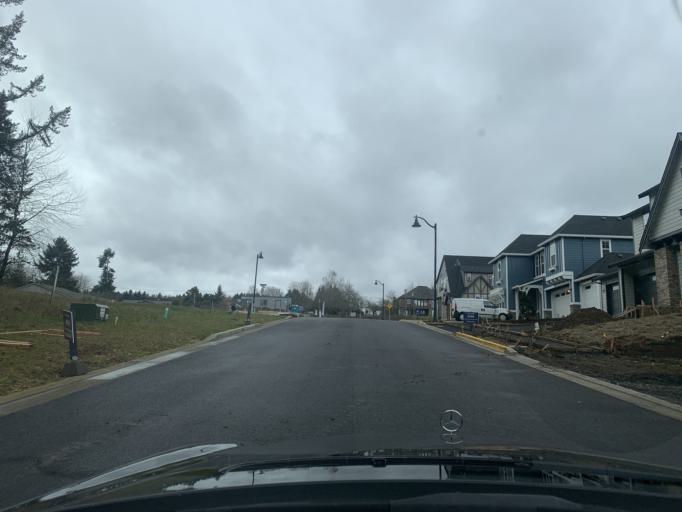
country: US
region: Oregon
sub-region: Clackamas County
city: Happy Valley
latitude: 45.4398
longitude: -122.5090
